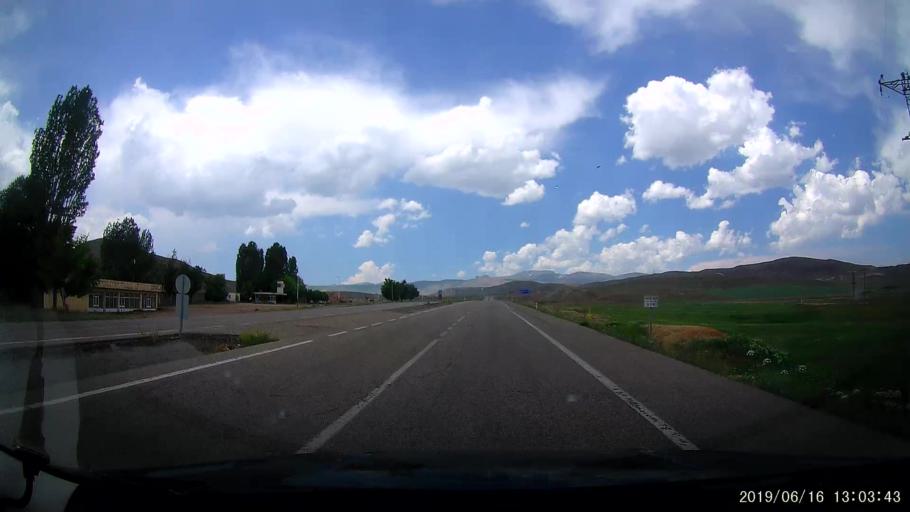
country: TR
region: Agri
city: Sulucem
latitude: 39.5845
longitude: 43.7853
